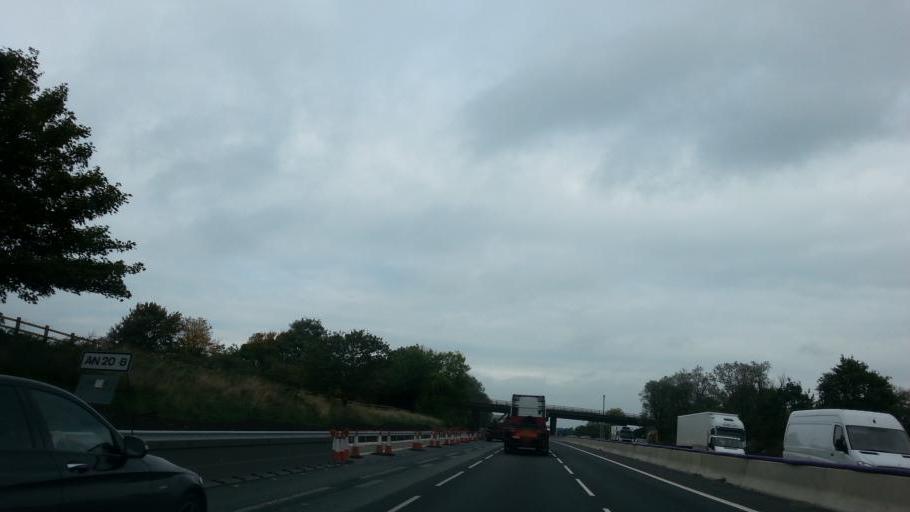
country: GB
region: England
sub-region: Cheshire East
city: Sandbach
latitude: 53.1722
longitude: -2.3601
